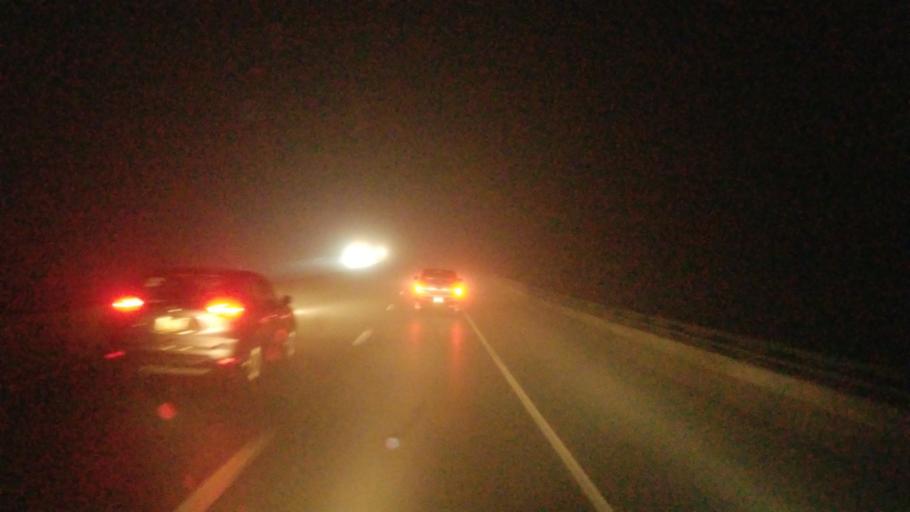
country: US
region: Pennsylvania
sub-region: Butler County
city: Meridian
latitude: 40.8843
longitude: -79.9665
